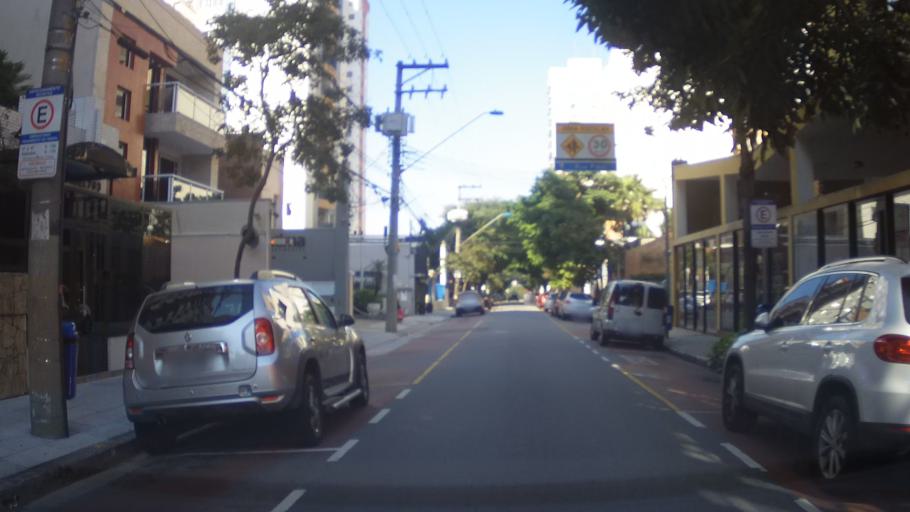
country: BR
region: Sao Paulo
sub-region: Sao Caetano Do Sul
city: Sao Caetano do Sul
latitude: -23.6190
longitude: -46.5642
